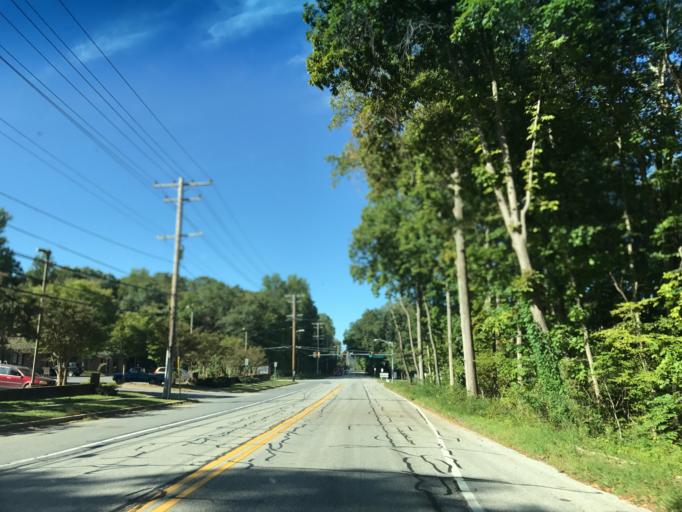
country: US
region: Maryland
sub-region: Anne Arundel County
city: Davidsonville
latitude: 38.9121
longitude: -76.6596
